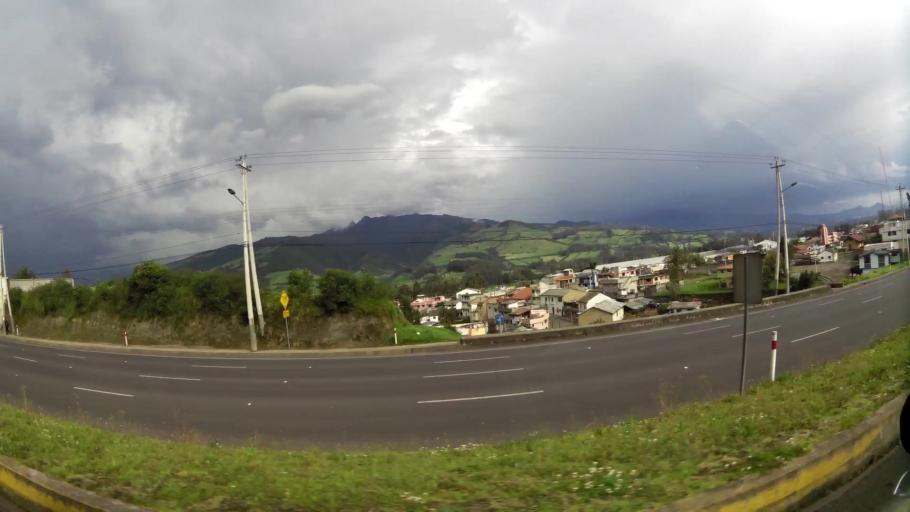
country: EC
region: Pichincha
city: Machachi
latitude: -0.4019
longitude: -78.5450
